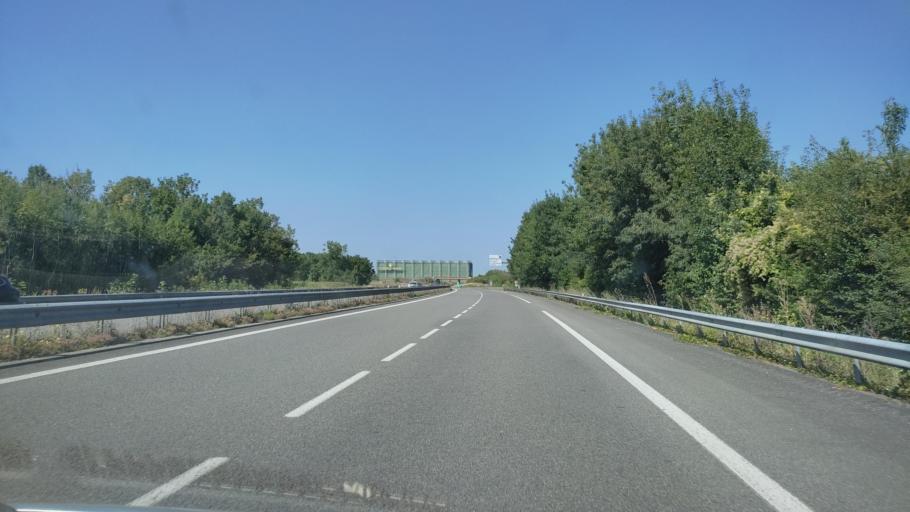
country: FR
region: Poitou-Charentes
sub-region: Departement de la Charente
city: Jarnac
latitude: 45.6877
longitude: -0.1377
